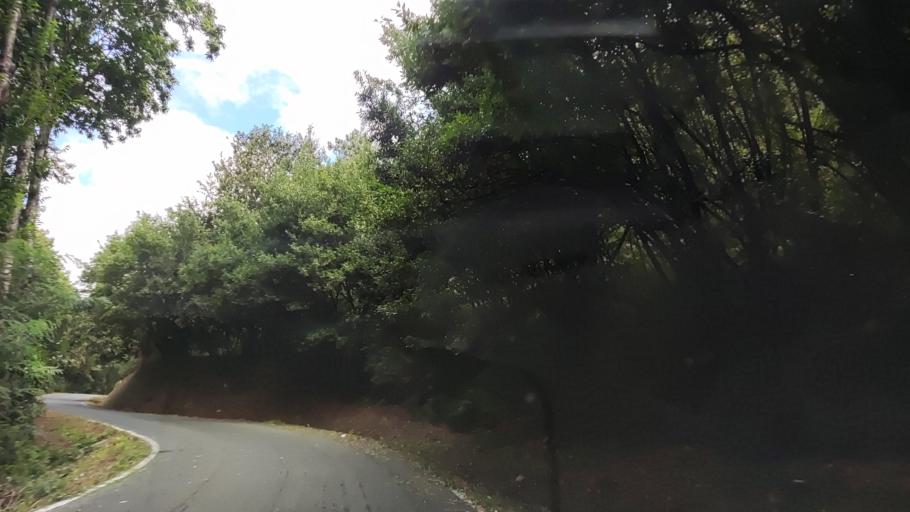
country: ES
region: Galicia
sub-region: Provincia da Coruna
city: Rois
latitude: 42.7443
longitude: -8.6982
